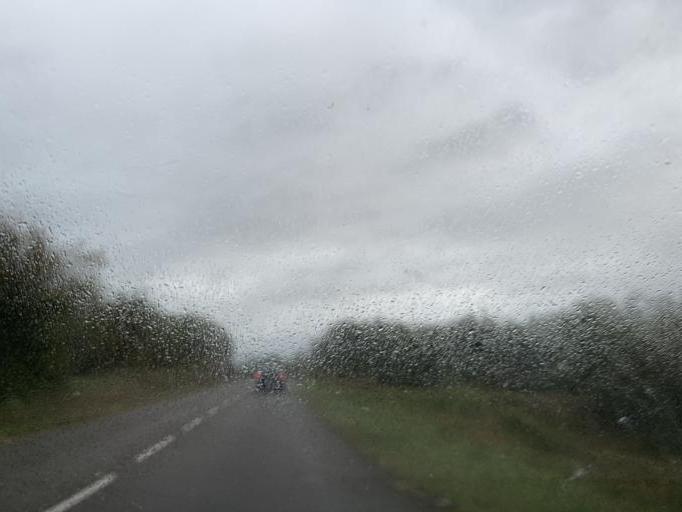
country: FR
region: Rhone-Alpes
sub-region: Departement de l'Ain
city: Belley
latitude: 45.7007
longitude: 5.6498
